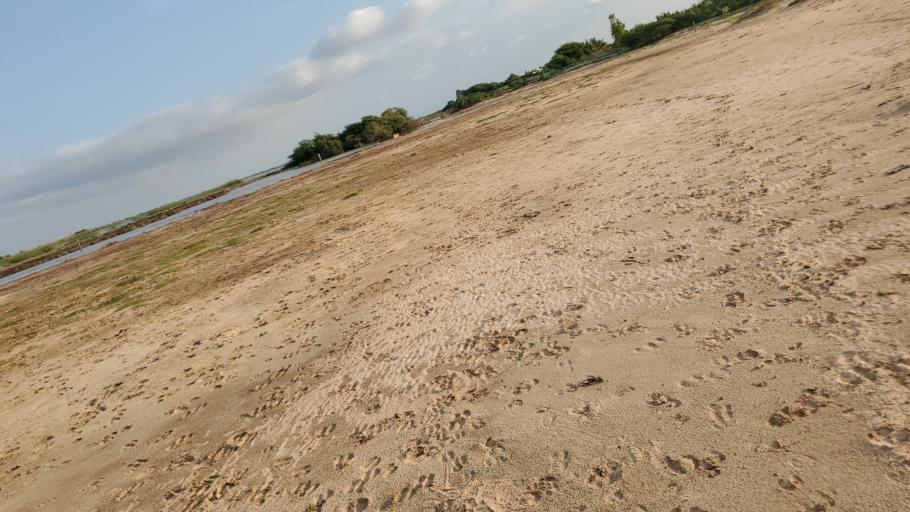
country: SN
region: Saint-Louis
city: Saint-Louis
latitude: 16.0457
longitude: -16.4166
